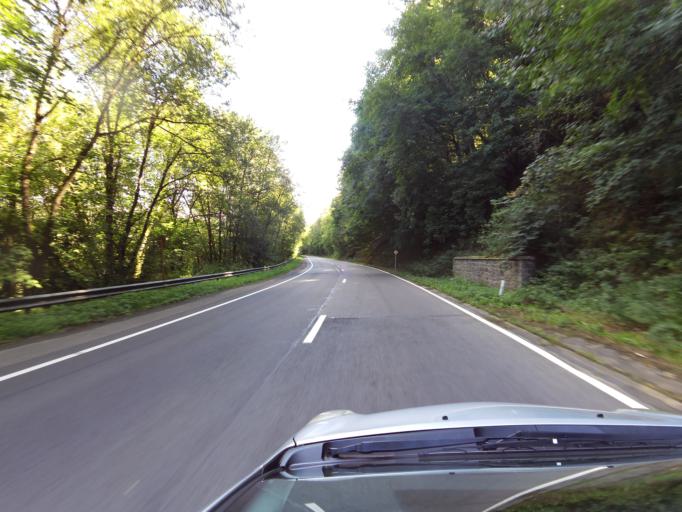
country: BE
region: Wallonia
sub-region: Province du Luxembourg
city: Rendeux
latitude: 50.2073
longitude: 5.5242
